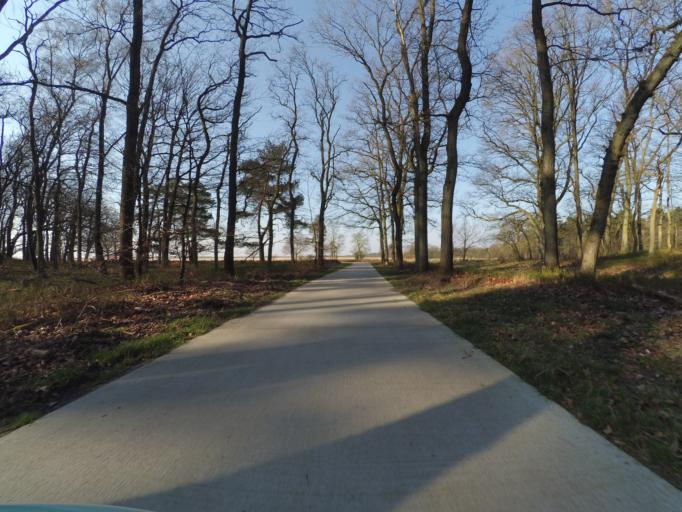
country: NL
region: Gelderland
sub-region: Gemeente Ede
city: Otterlo
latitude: 52.1041
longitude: 5.8723
